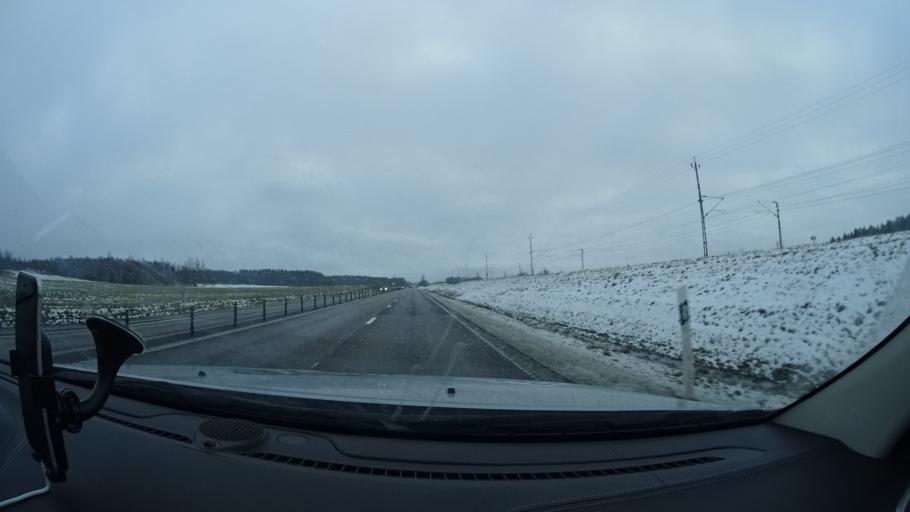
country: SE
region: OEstergoetland
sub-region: Motala Kommun
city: Stenstorp
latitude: 58.4368
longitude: 15.0584
